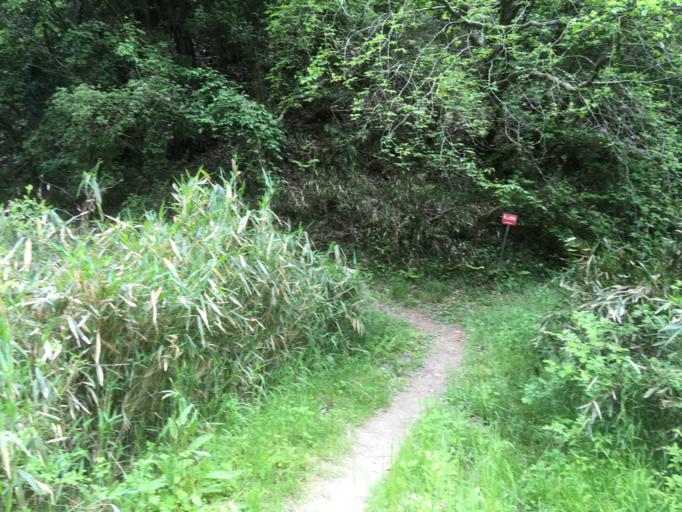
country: JP
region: Nara
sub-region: Ikoma-shi
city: Ikoma
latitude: 34.7022
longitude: 135.6723
